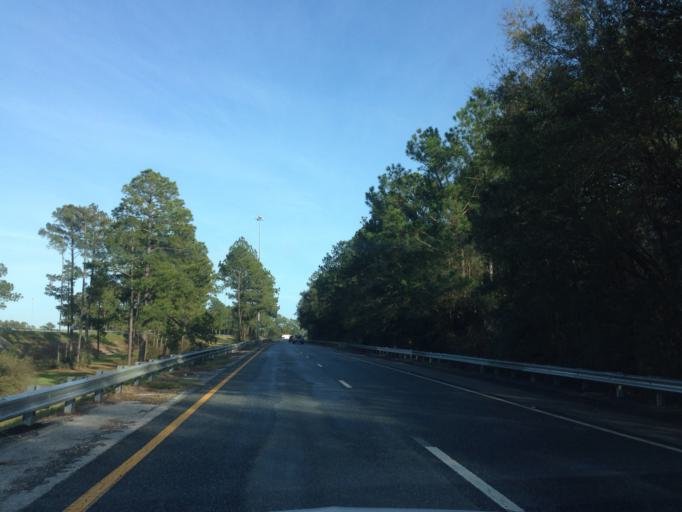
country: US
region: Florida
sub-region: Escambia County
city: Ensley
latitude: 30.5341
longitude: -87.3361
